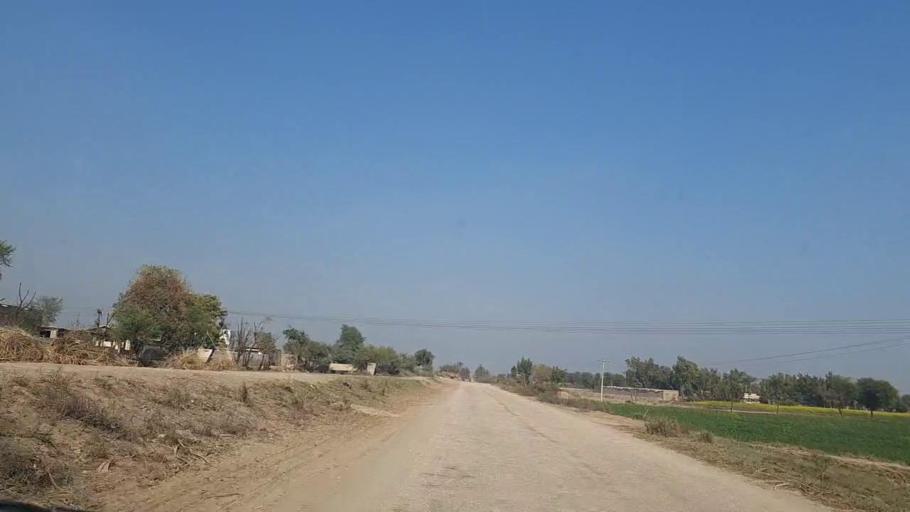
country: PK
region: Sindh
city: Sakrand
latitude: 26.0614
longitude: 68.3468
